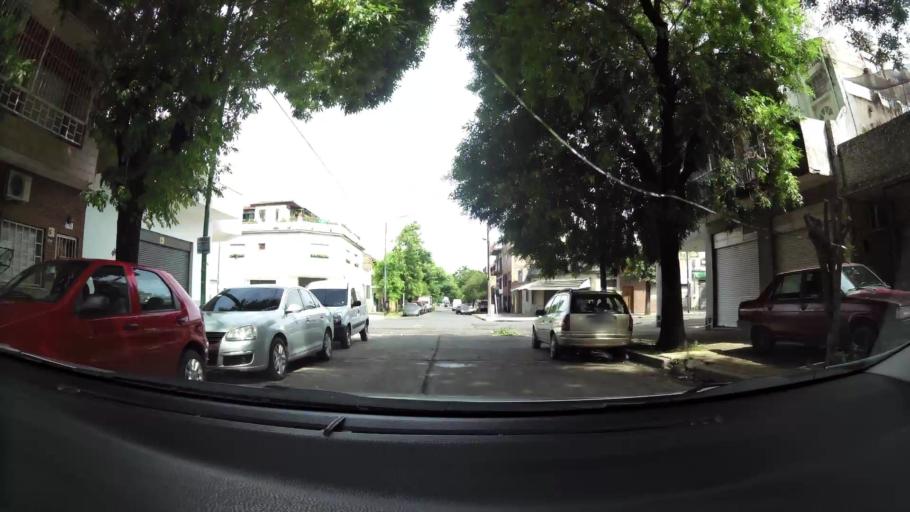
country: AR
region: Buenos Aires F.D.
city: Villa Lugano
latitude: -34.6575
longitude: -58.4313
